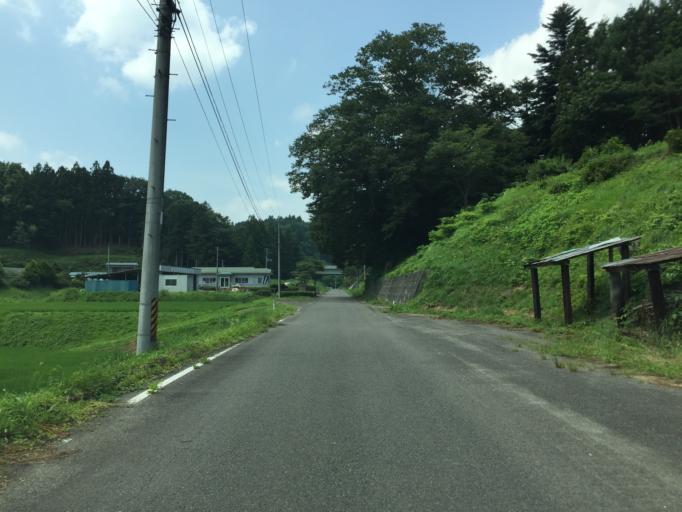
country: JP
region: Fukushima
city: Ishikawa
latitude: 37.2278
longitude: 140.5543
